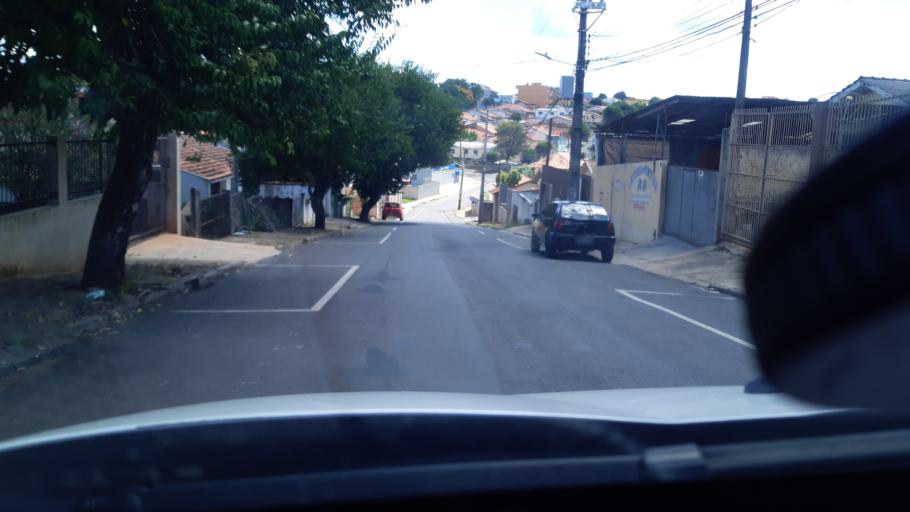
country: BR
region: Parana
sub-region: Telemaco Borba
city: Telemaco Borba
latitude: -24.3231
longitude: -50.6346
